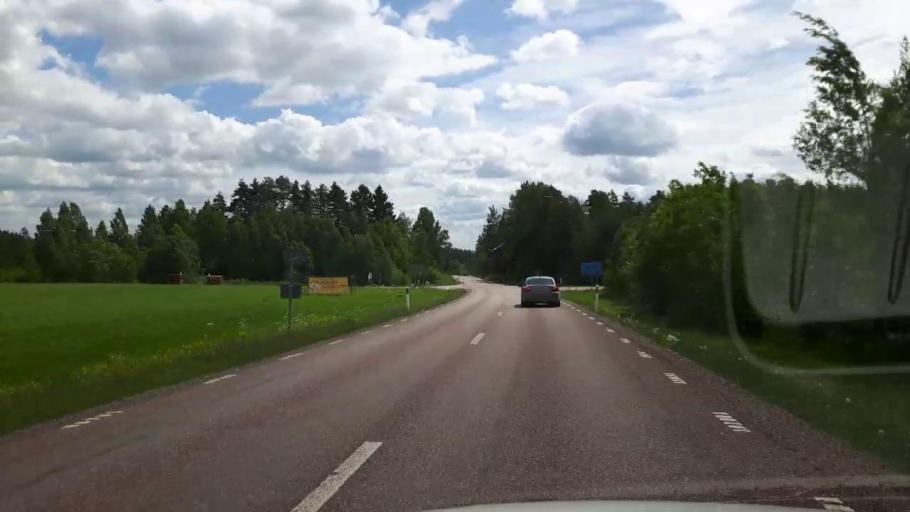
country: SE
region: Dalarna
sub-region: Saters Kommun
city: Saeter
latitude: 60.4236
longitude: 15.8413
